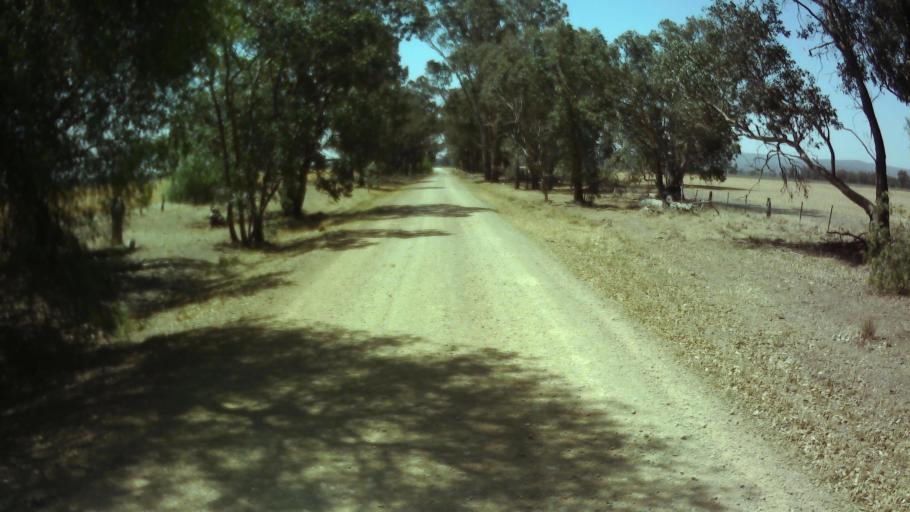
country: AU
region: New South Wales
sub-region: Weddin
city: Grenfell
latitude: -34.0307
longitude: 147.8993
